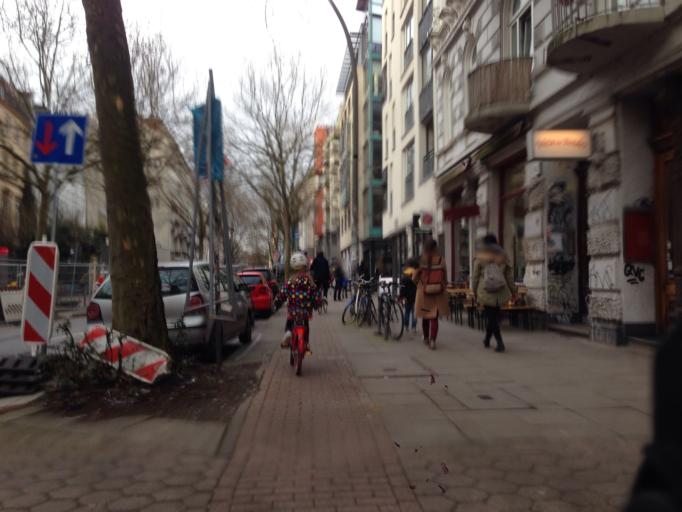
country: DE
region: Hamburg
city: St. Pauli
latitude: 53.5596
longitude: 9.9644
